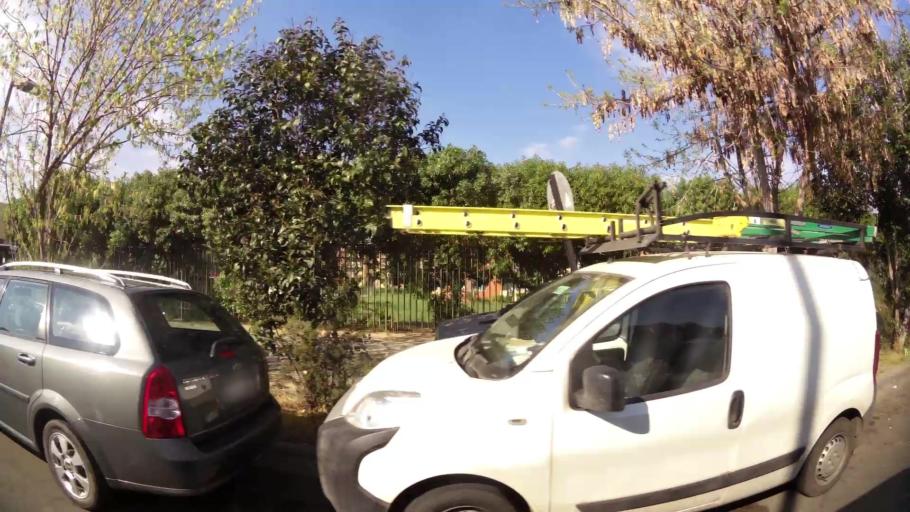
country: CL
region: Santiago Metropolitan
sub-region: Provincia de Santiago
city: Lo Prado
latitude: -33.4517
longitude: -70.7628
